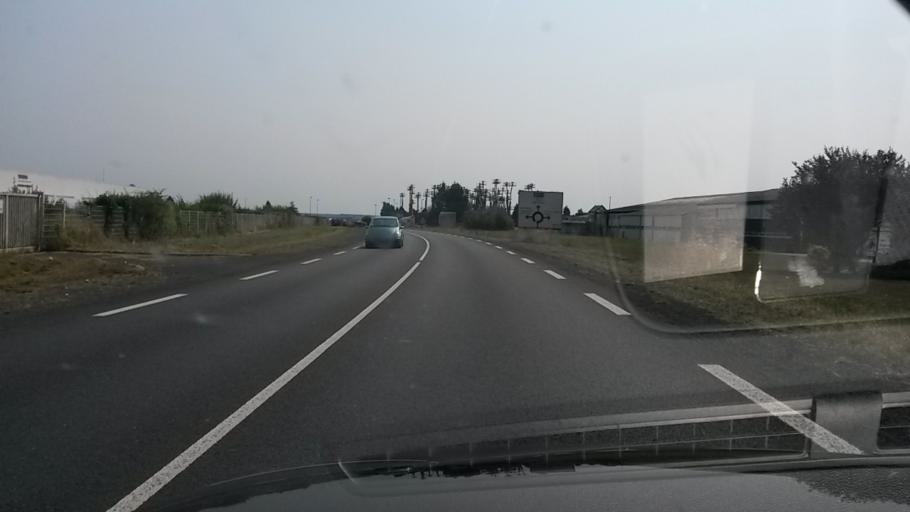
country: FR
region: Pays de la Loire
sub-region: Departement de la Loire-Atlantique
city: Mesanger
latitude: 47.4130
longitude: -1.1900
